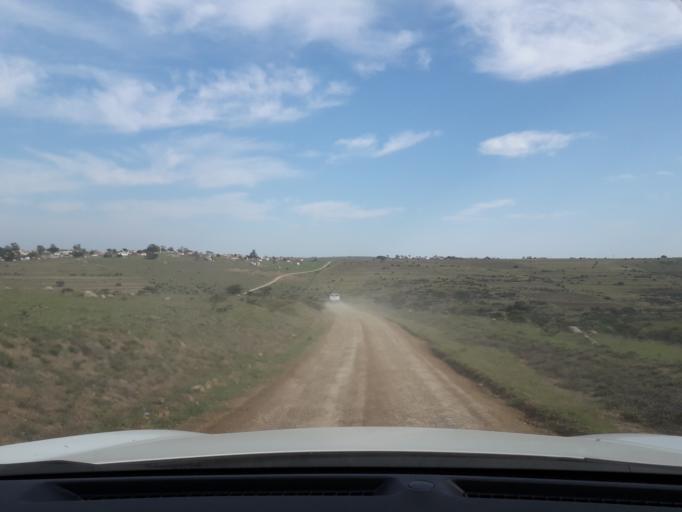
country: ZA
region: Eastern Cape
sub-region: Buffalo City Metropolitan Municipality
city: Bhisho
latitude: -32.9942
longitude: 27.3423
